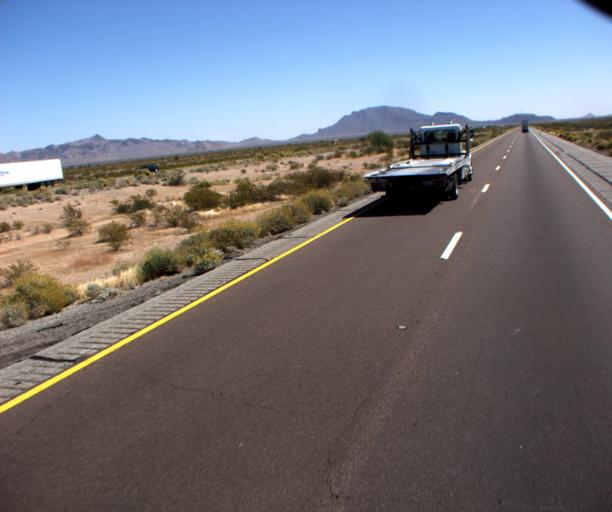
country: US
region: Arizona
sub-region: La Paz County
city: Salome
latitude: 33.5451
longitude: -113.1976
